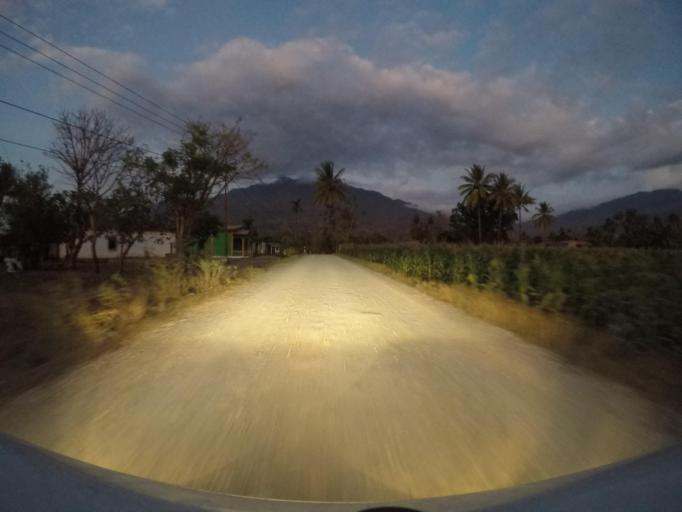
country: TL
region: Bobonaro
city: Maliana
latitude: -8.9808
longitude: 125.2160
